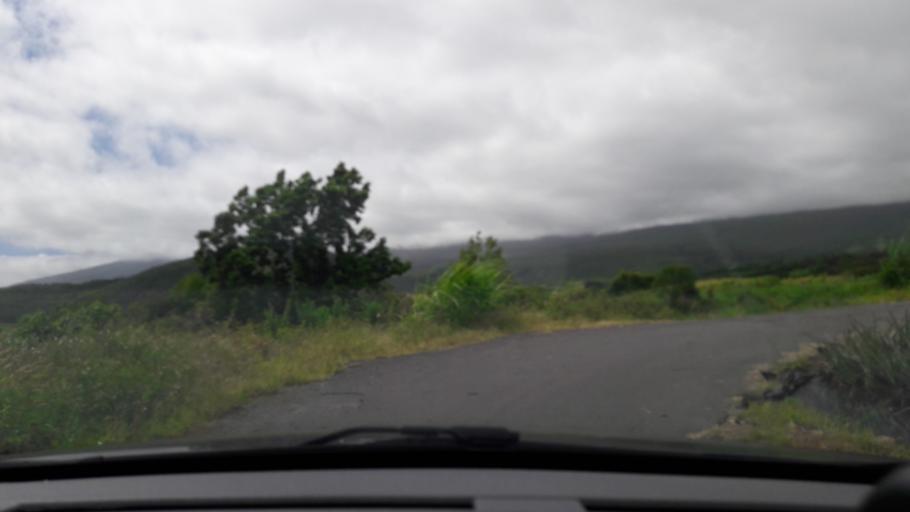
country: RE
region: Reunion
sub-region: Reunion
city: Saint-Benoit
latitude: -21.0961
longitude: 55.7001
